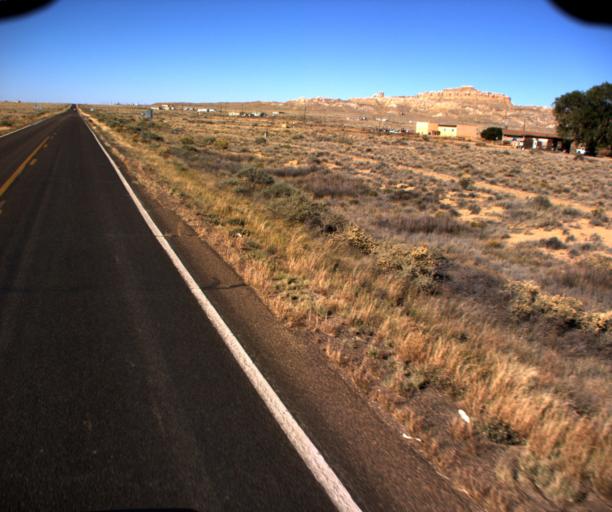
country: US
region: Arizona
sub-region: Navajo County
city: First Mesa
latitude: 35.7971
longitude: -110.4629
